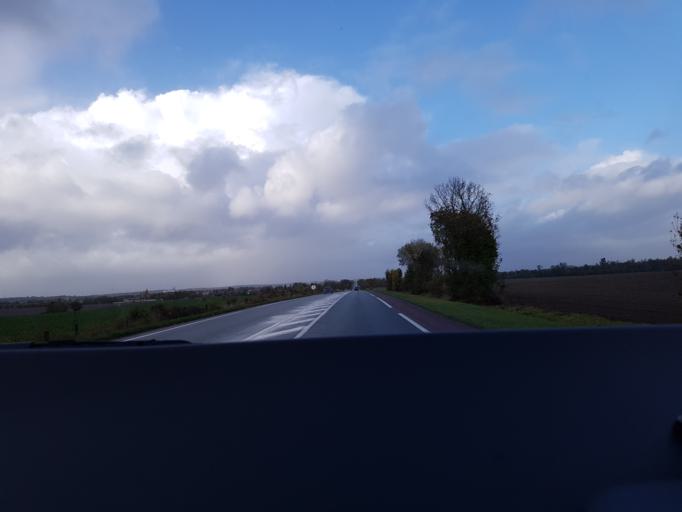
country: FR
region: Poitou-Charentes
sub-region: Departement de la Charente-Maritime
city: Les Gonds
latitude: 45.6866
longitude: -0.6124
